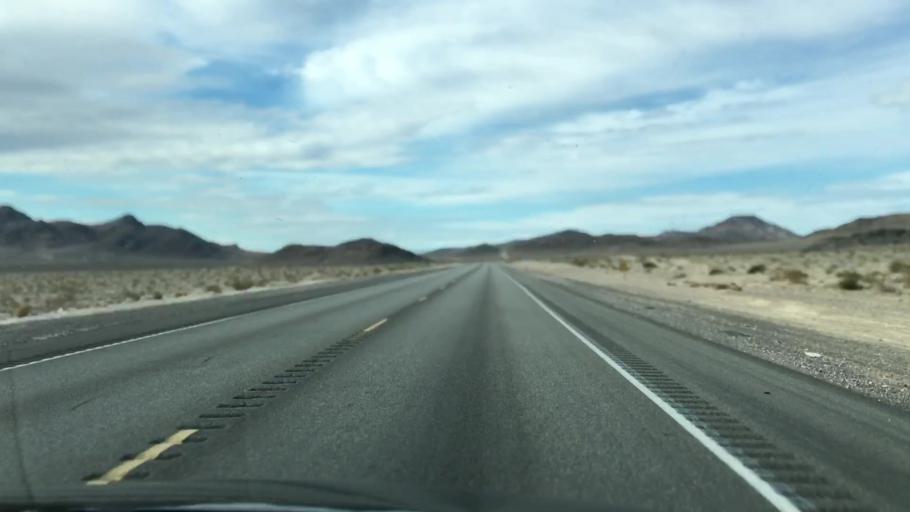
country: US
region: Nevada
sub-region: Nye County
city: Pahrump
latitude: 36.6180
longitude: -116.2879
